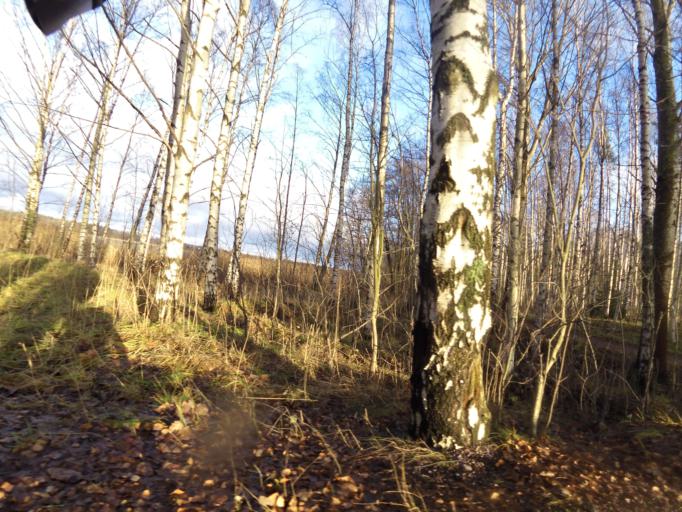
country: FI
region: Uusimaa
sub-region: Helsinki
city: Otaniemi
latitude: 60.1893
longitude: 24.8276
